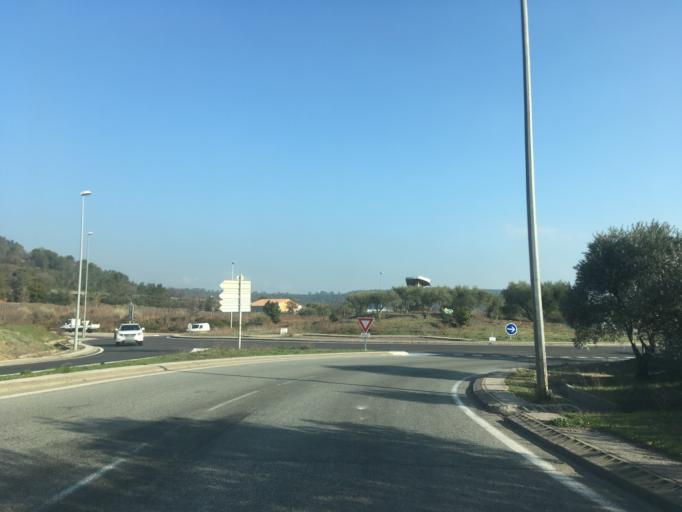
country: FR
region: Provence-Alpes-Cote d'Azur
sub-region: Departement du Var
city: Le Cannet-des-Maures
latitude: 43.3934
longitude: 6.3499
